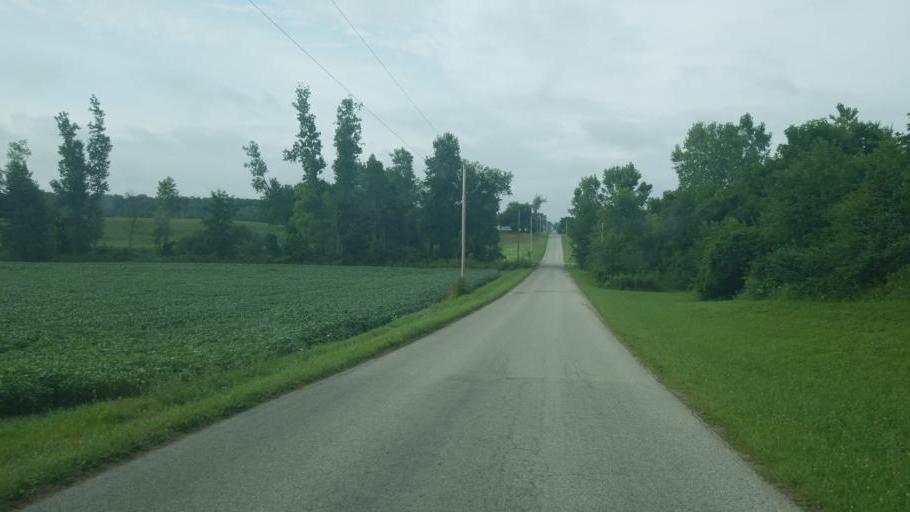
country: US
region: Ohio
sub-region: Knox County
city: Fredericktown
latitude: 40.4560
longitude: -82.6774
